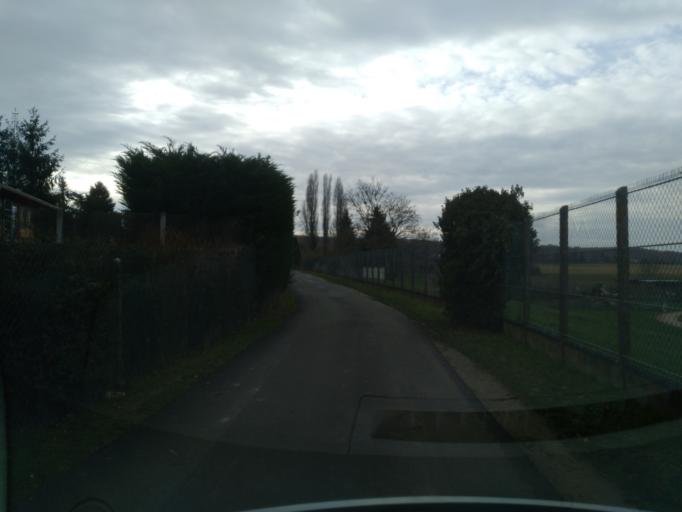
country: FR
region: Ile-de-France
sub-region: Departement des Yvelines
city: Fontenay-le-Fleury
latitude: 48.8181
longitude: 2.0407
